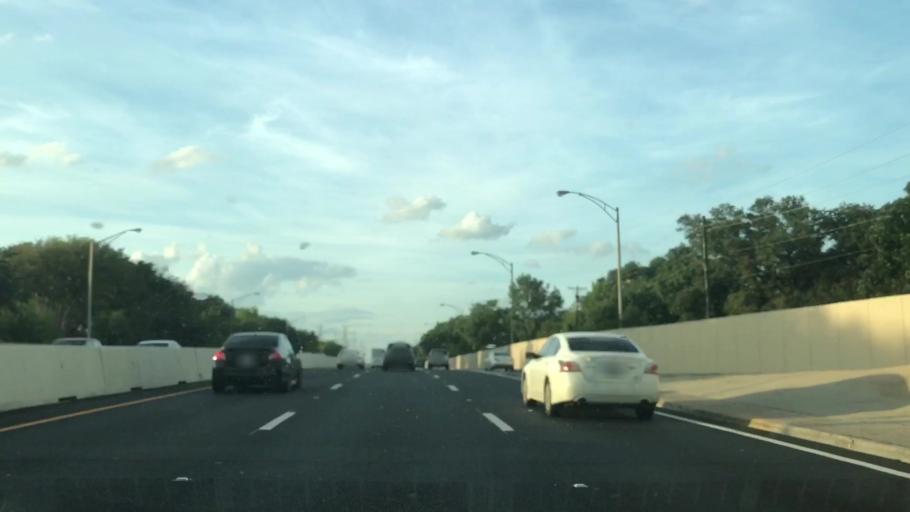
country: US
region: Texas
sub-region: Dallas County
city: University Park
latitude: 32.8966
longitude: -96.8098
